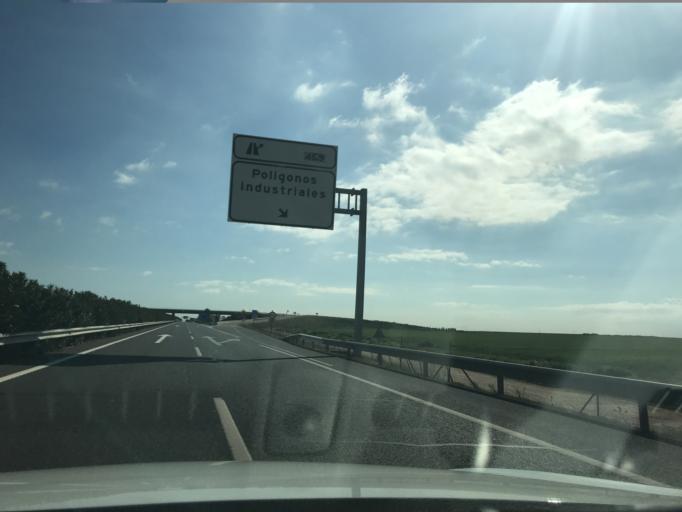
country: ES
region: Andalusia
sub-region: Provincia de Sevilla
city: Ecija
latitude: 37.5236
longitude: -5.1367
